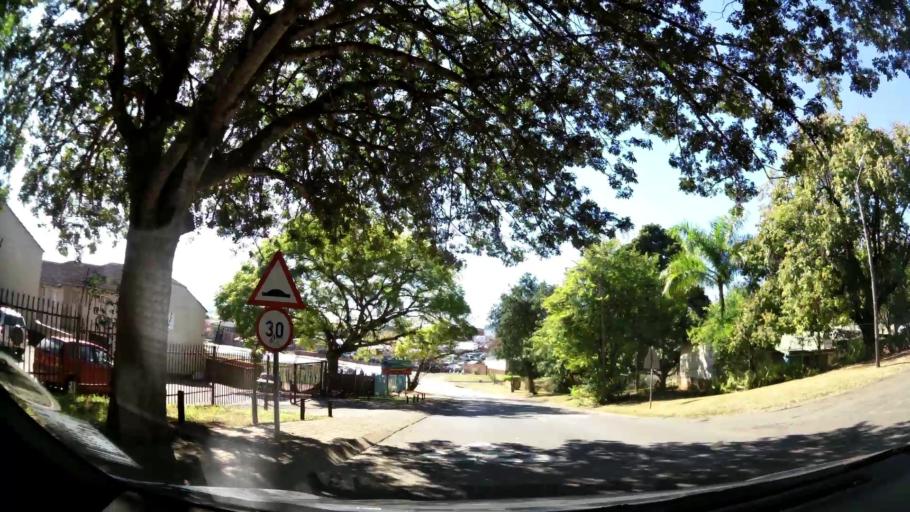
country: ZA
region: Limpopo
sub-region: Mopani District Municipality
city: Tzaneen
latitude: -23.8283
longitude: 30.1566
